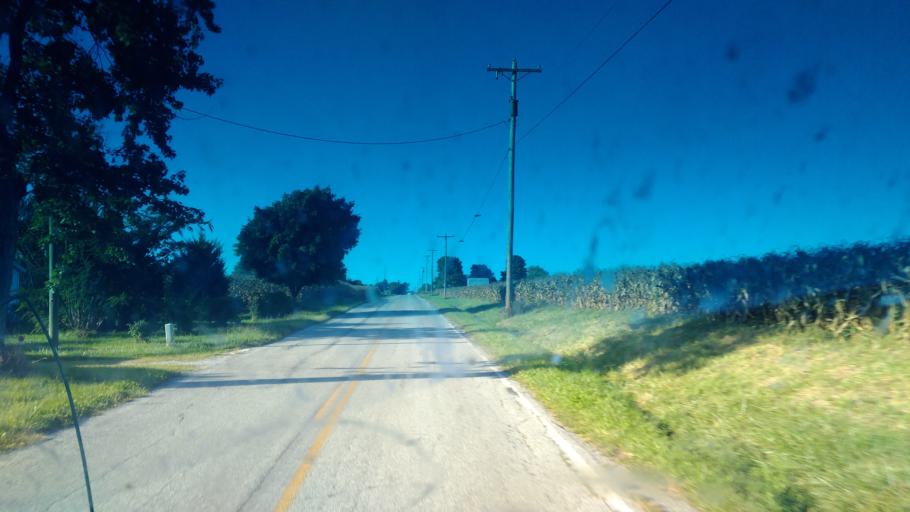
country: US
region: Ohio
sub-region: Wyandot County
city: Carey
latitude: 40.9392
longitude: -83.4861
